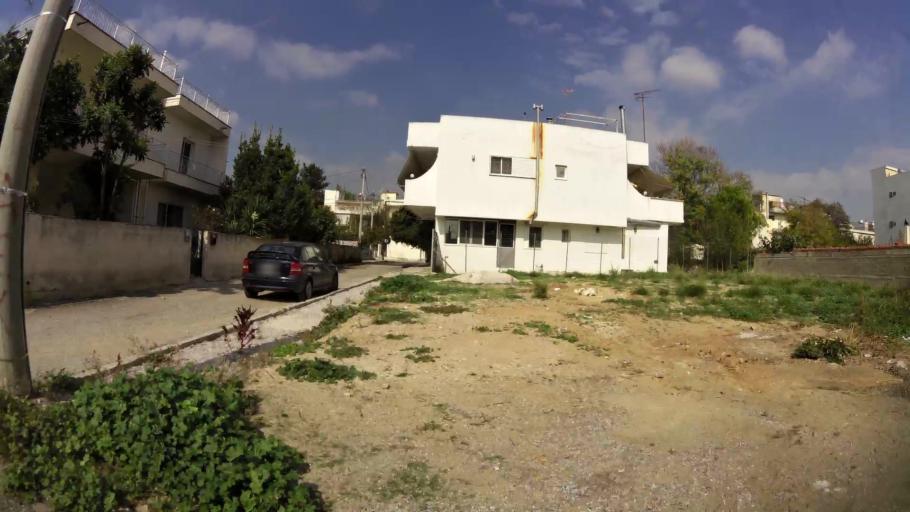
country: GR
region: Attica
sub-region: Nomarchia Dytikis Attikis
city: Zefyri
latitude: 38.0678
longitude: 23.7139
